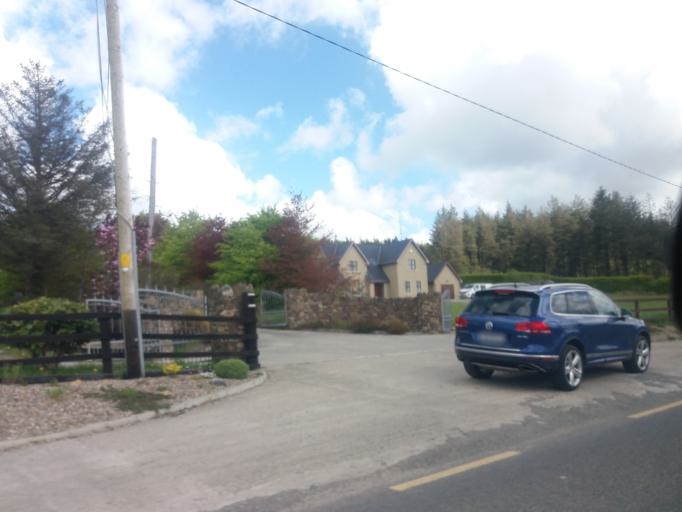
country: IE
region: Leinster
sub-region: Loch Garman
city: Loch Garman
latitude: 52.2926
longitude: -6.5822
